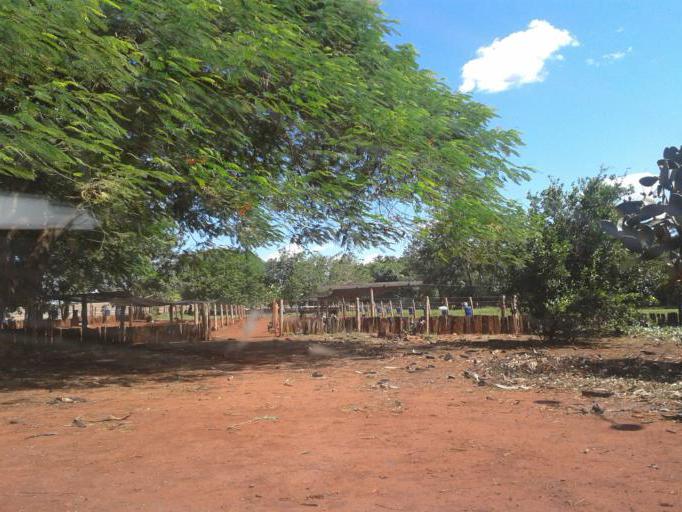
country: BR
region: Minas Gerais
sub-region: Capinopolis
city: Capinopolis
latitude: -18.6508
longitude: -49.5723
